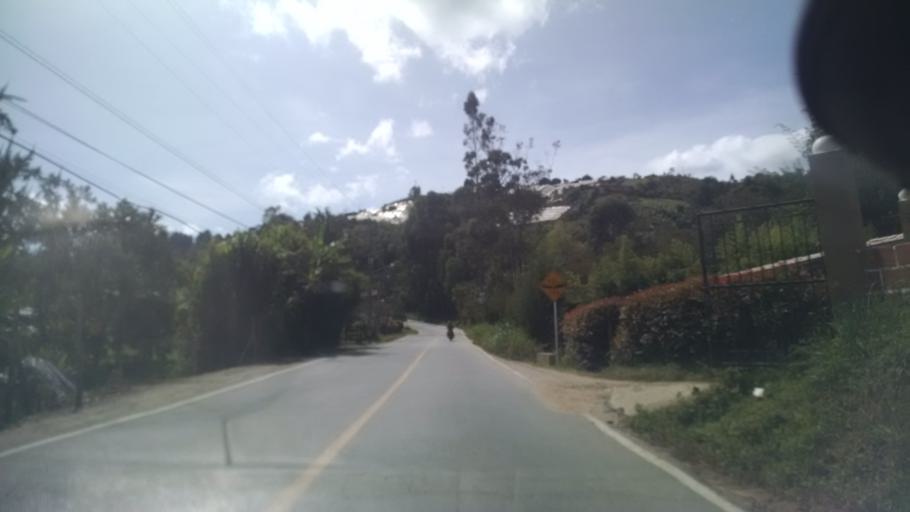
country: CO
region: Antioquia
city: San Vicente
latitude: 6.2244
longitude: -75.2525
